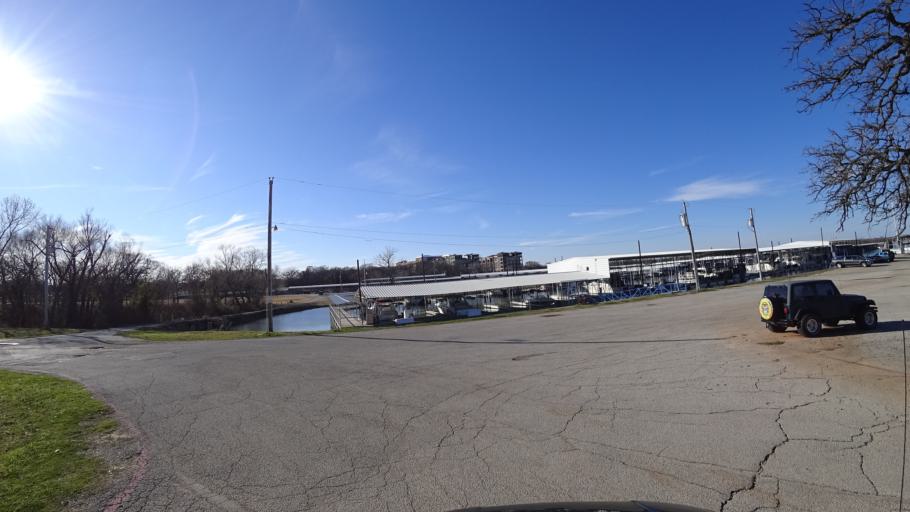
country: US
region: Texas
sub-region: Denton County
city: Highland Village
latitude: 33.0846
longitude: -97.0212
